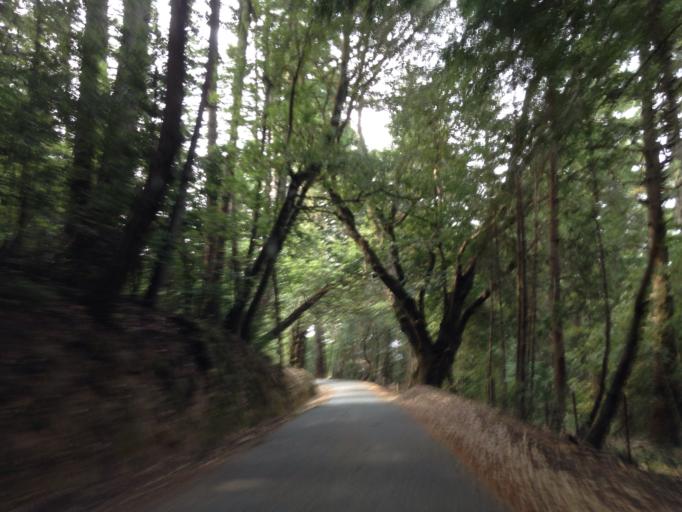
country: US
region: California
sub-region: San Mateo County
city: Woodside
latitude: 37.3879
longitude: -122.2980
